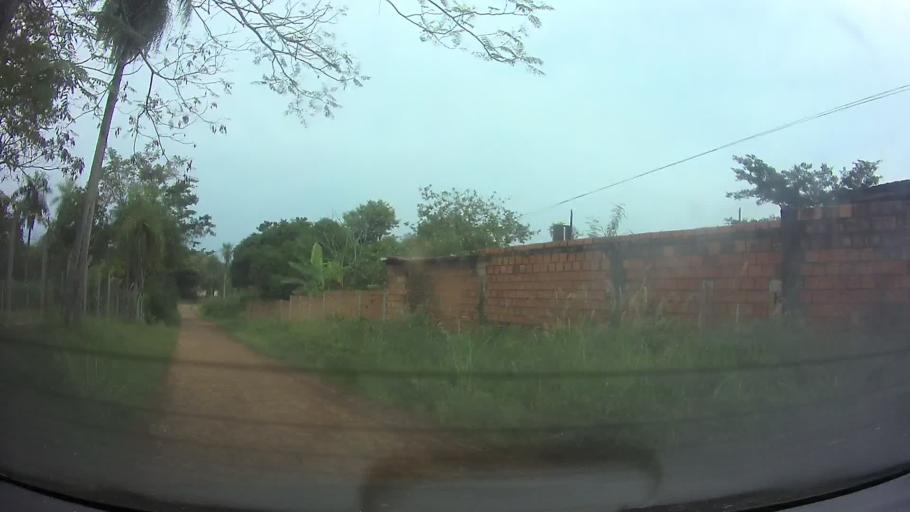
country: PY
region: Central
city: Limpio
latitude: -25.2381
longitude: -57.4616
